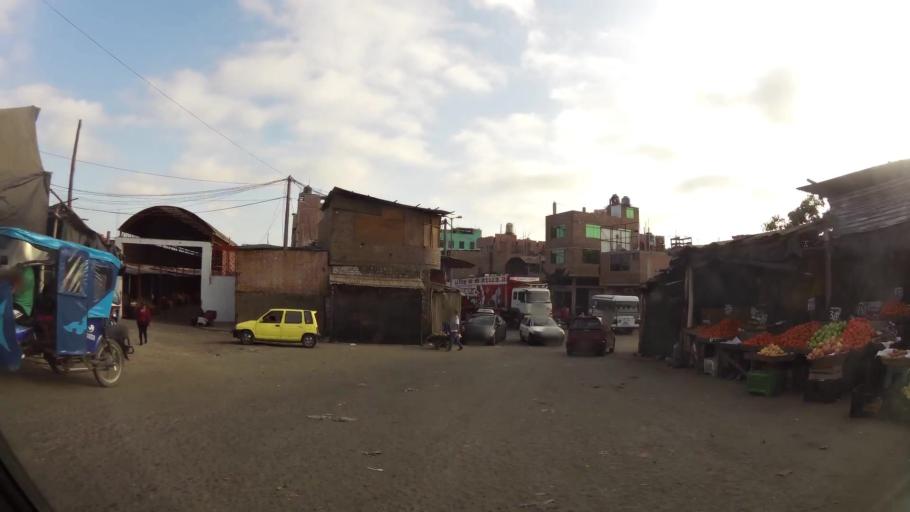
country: PE
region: La Libertad
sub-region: Provincia de Trujillo
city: La Esperanza
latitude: -8.0892
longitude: -79.0237
